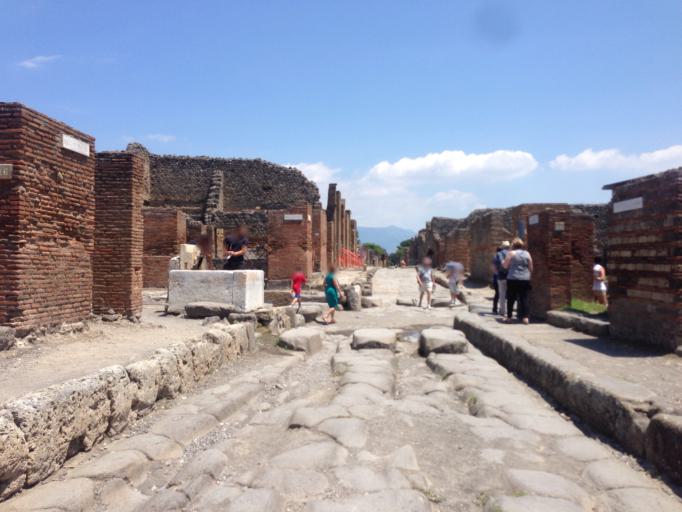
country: IT
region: Campania
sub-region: Provincia di Napoli
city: Pompei
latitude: 40.7515
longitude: 14.4860
